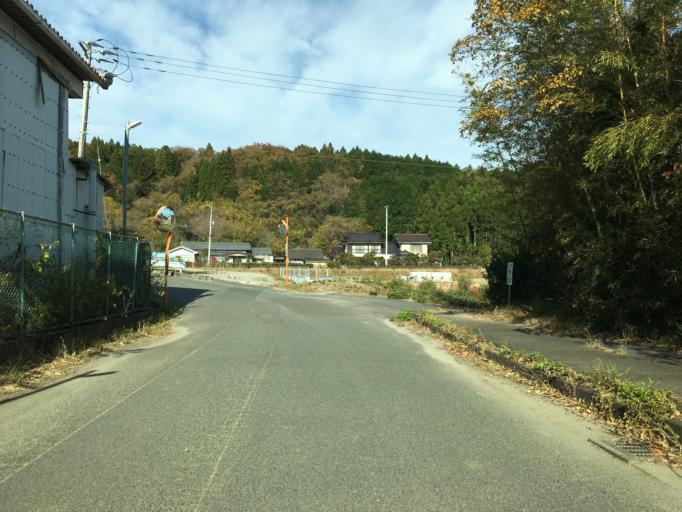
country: JP
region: Miyagi
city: Watari
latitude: 37.9212
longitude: 140.8900
